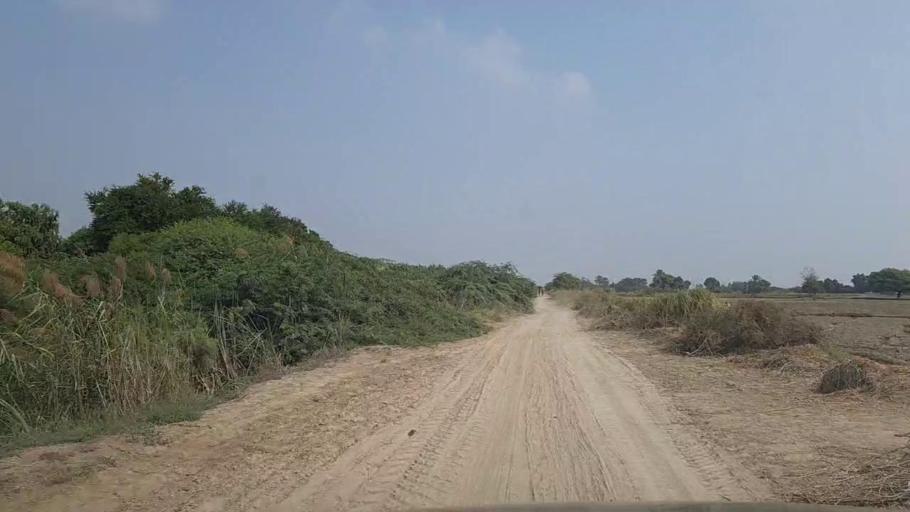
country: PK
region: Sindh
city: Thatta
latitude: 24.7692
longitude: 67.8224
